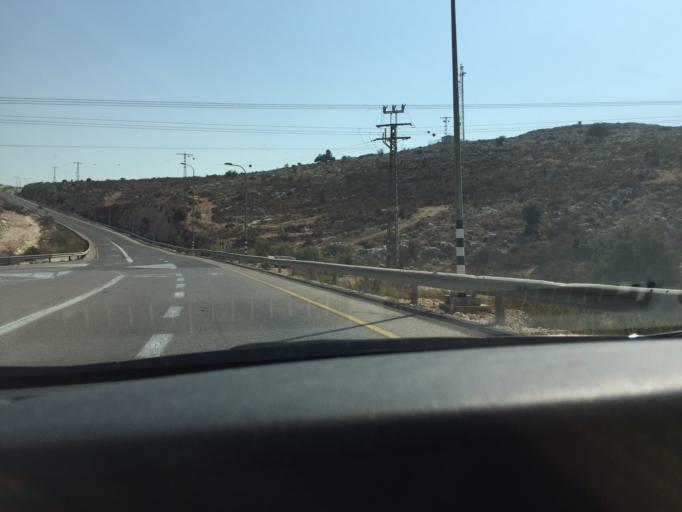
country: PS
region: West Bank
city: Sartah
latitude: 32.0906
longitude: 35.1032
